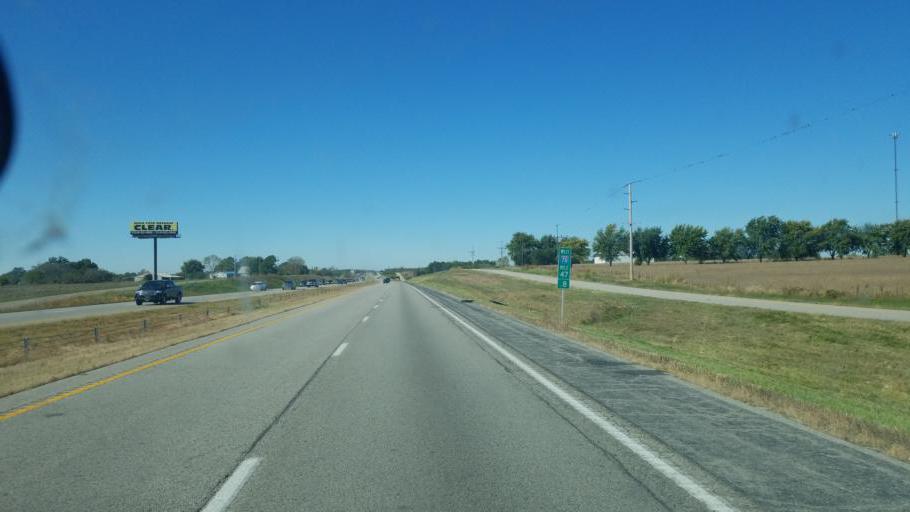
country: US
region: Missouri
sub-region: Lafayette County
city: Higginsville
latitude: 39.0016
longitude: -93.7609
